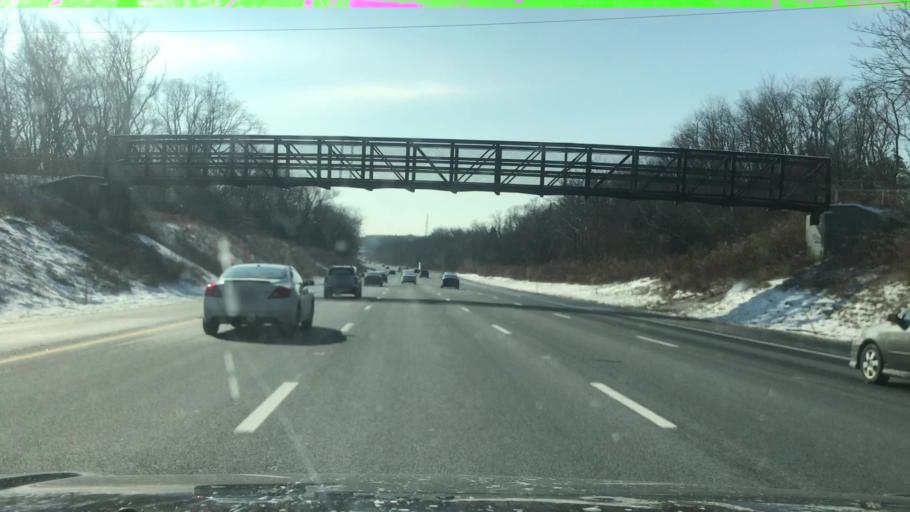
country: US
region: New Jersey
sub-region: Monmouth County
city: Ramtown
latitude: 40.1474
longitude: -74.1087
